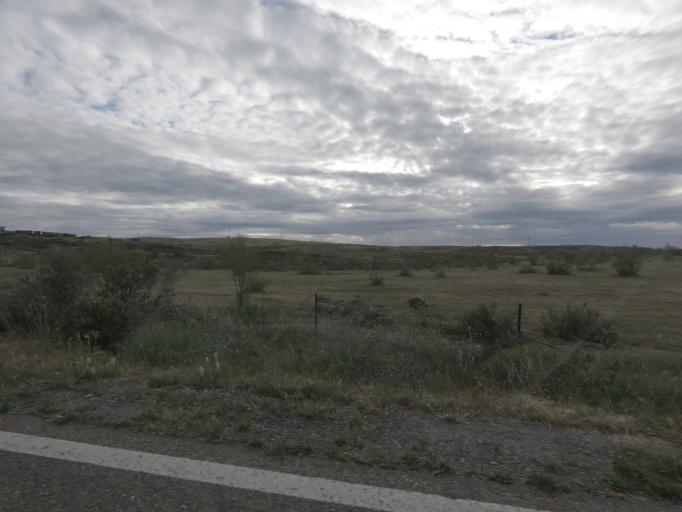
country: ES
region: Extremadura
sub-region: Provincia de Caceres
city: Coria
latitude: 39.9446
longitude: -6.5079
